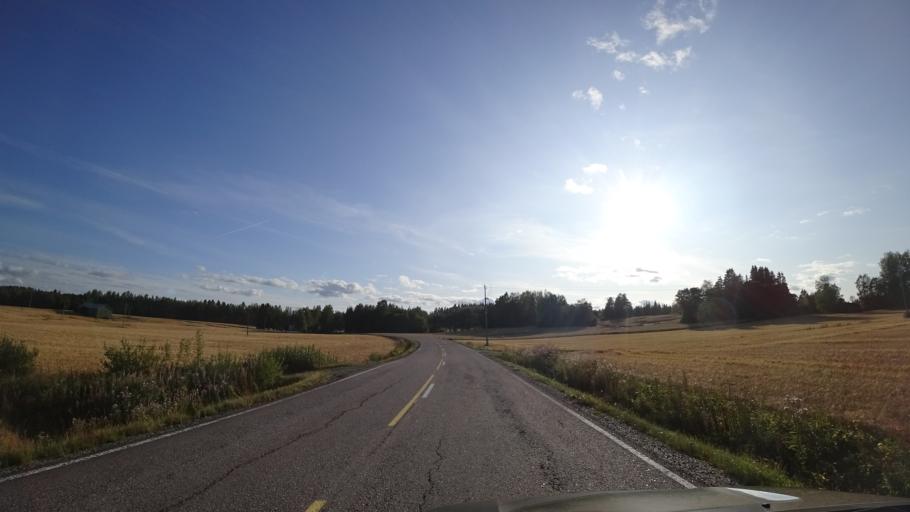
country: FI
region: Paijanne Tavastia
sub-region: Lahti
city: Asikkala
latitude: 61.1818
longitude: 25.3814
